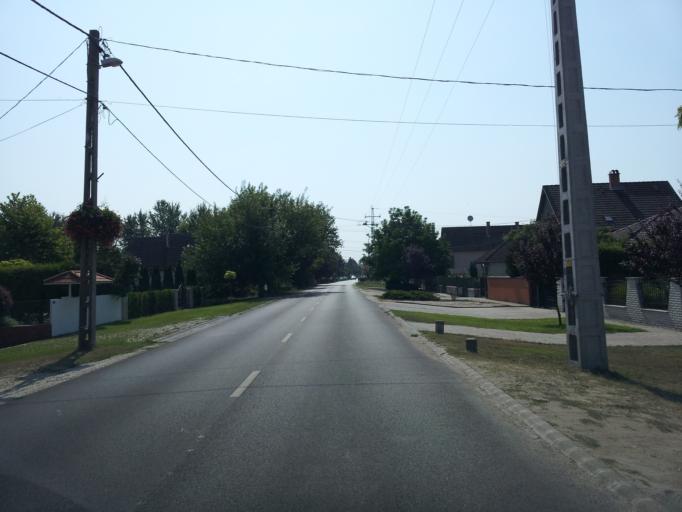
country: HU
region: Pest
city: Dunavarsany
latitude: 47.2842
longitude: 19.0560
